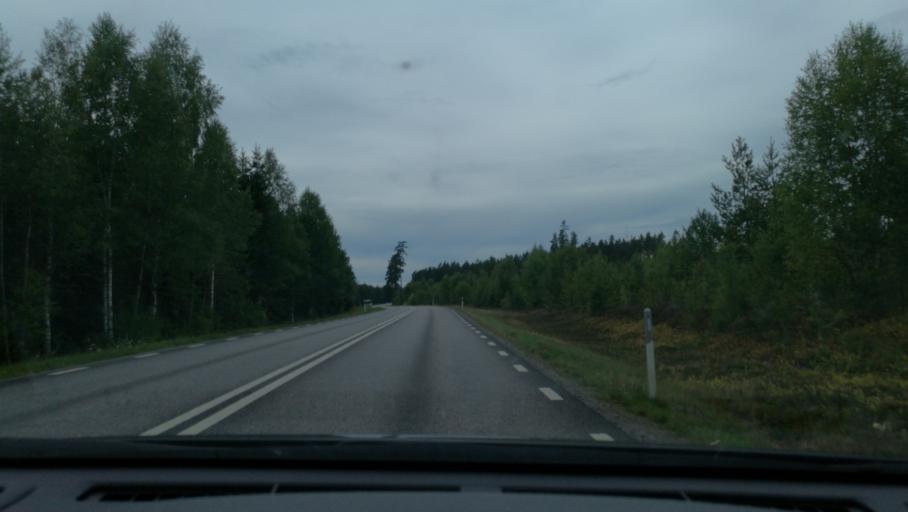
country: SE
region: Soedermanland
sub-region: Katrineholms Kommun
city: Katrineholm
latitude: 59.1168
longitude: 16.1629
